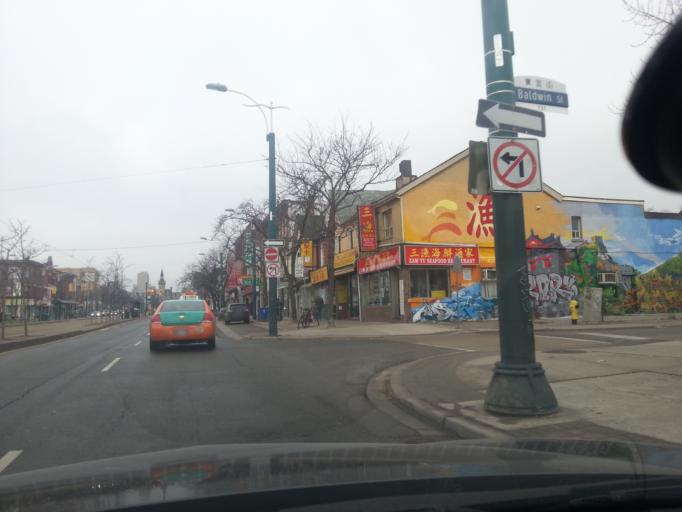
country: CA
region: Ontario
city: Toronto
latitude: 43.6548
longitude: -79.3987
